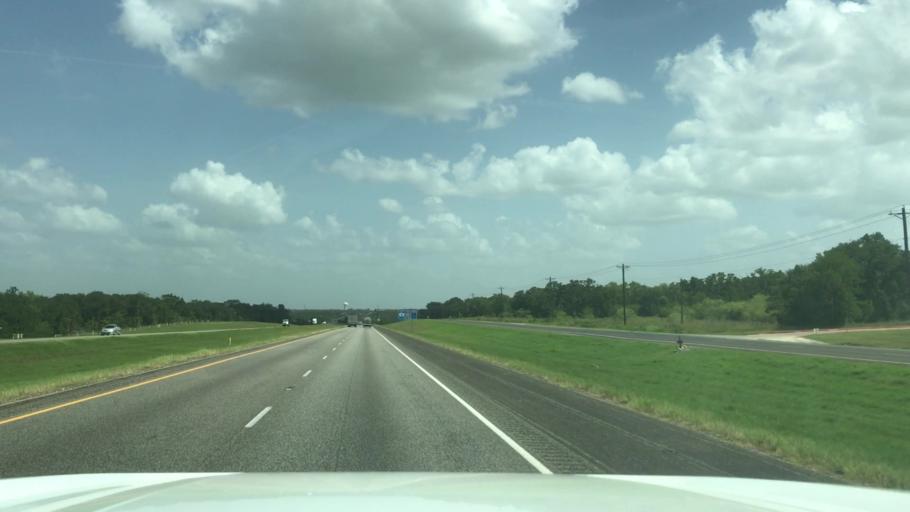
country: US
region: Texas
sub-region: Brazos County
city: Bryan
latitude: 30.7371
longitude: -96.4388
